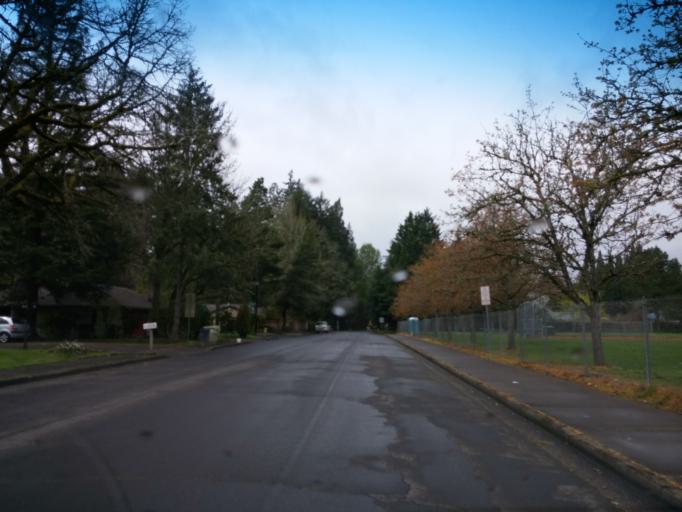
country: US
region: Oregon
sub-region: Washington County
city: Aloha
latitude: 45.5036
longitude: -122.8549
